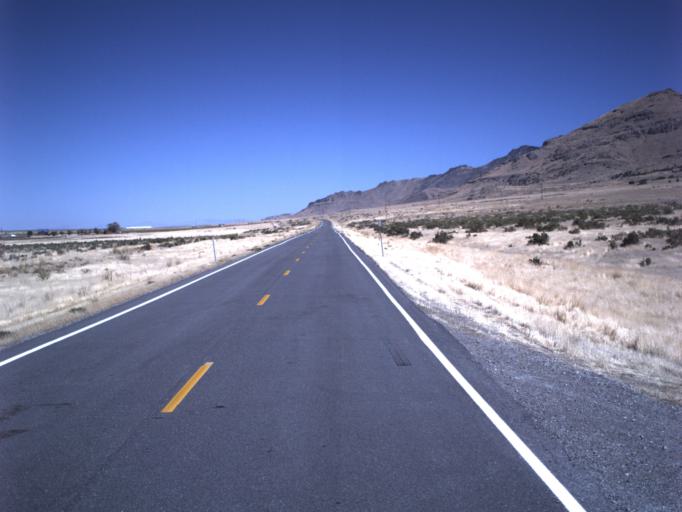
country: US
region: Utah
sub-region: Tooele County
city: Grantsville
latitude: 40.6621
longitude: -112.6781
